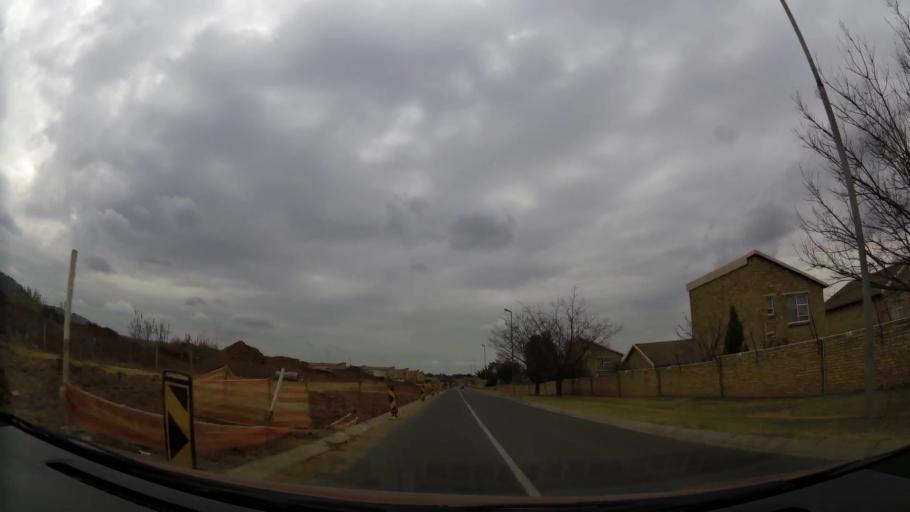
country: ZA
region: Gauteng
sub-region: City of Johannesburg Metropolitan Municipality
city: Roodepoort
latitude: -26.1097
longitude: 27.8909
